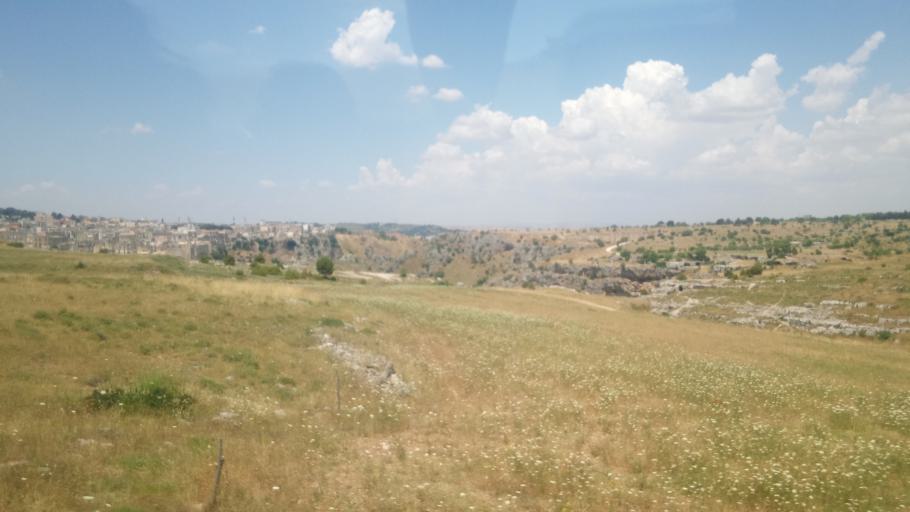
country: IT
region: Basilicate
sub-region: Provincia di Matera
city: Matera
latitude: 40.6656
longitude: 16.6206
